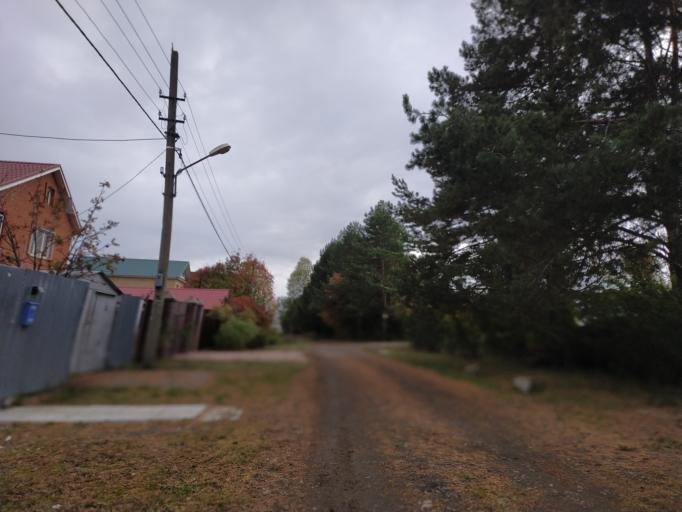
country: RU
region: Chuvashia
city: Ishley
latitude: 56.1281
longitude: 47.0913
